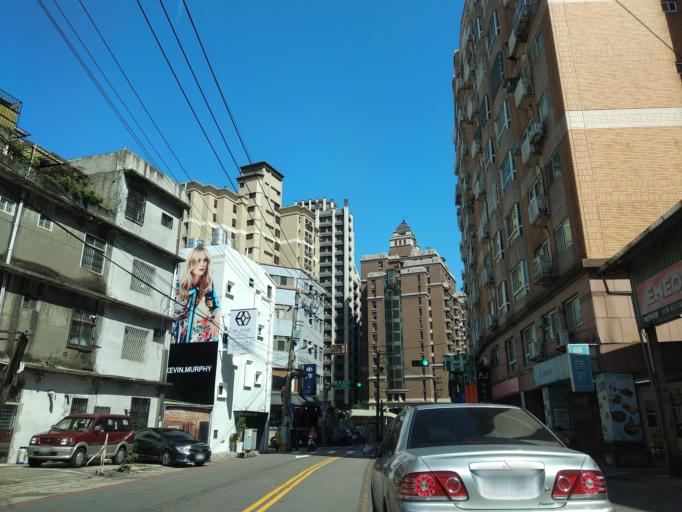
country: TW
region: Taiwan
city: Taoyuan City
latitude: 24.9523
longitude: 121.2272
